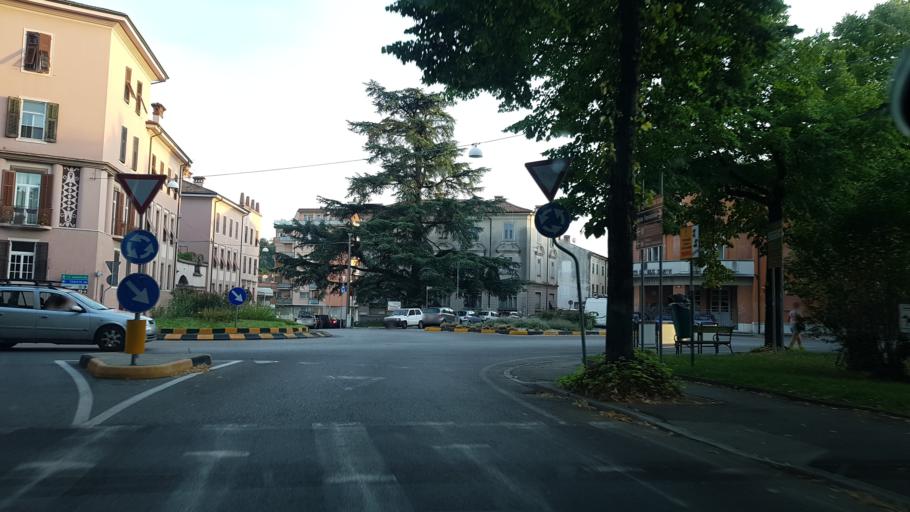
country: IT
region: Friuli Venezia Giulia
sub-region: Provincia di Gorizia
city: Gorizia
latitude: 45.9513
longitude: 13.6284
